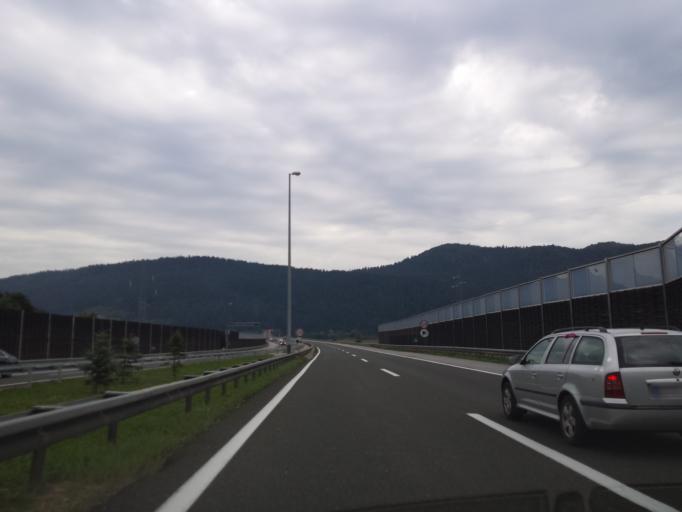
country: HR
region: Licko-Senjska
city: Otocac
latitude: 44.8696
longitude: 15.2073
